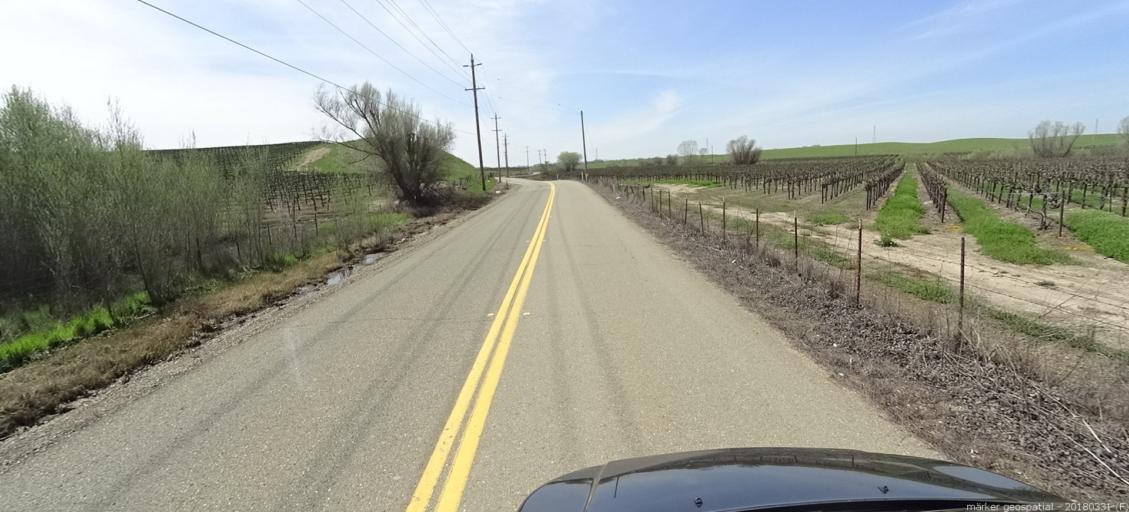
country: US
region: California
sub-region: Sacramento County
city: Rancho Murieta
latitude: 38.5147
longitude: -121.1322
